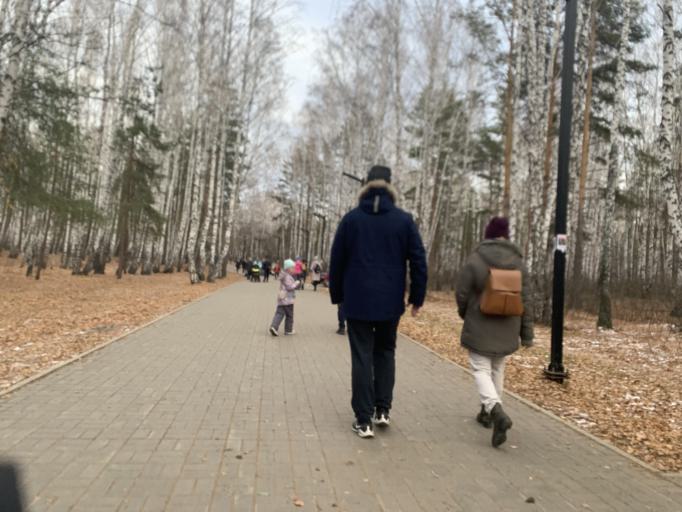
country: RU
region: Chelyabinsk
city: Roshchino
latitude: 55.1964
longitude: 61.2916
